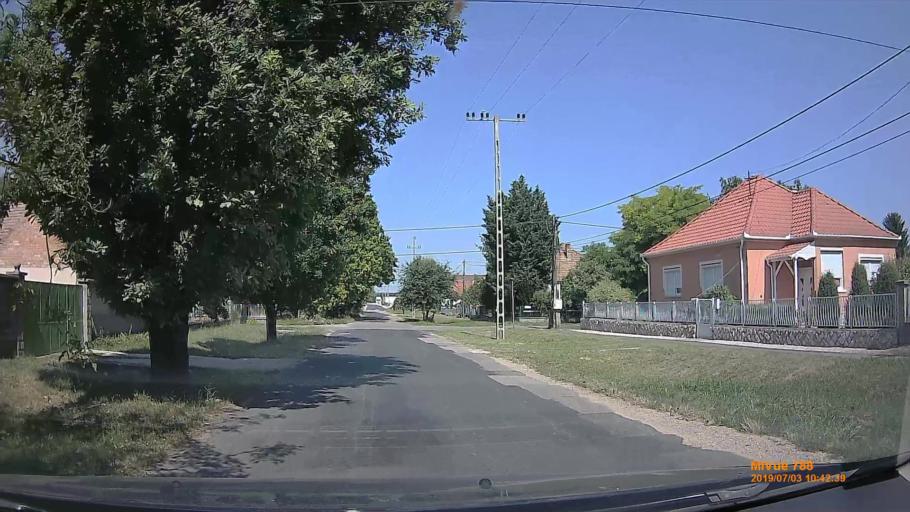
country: HU
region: Gyor-Moson-Sopron
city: Gyorujbarat
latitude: 47.6385
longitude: 17.6121
